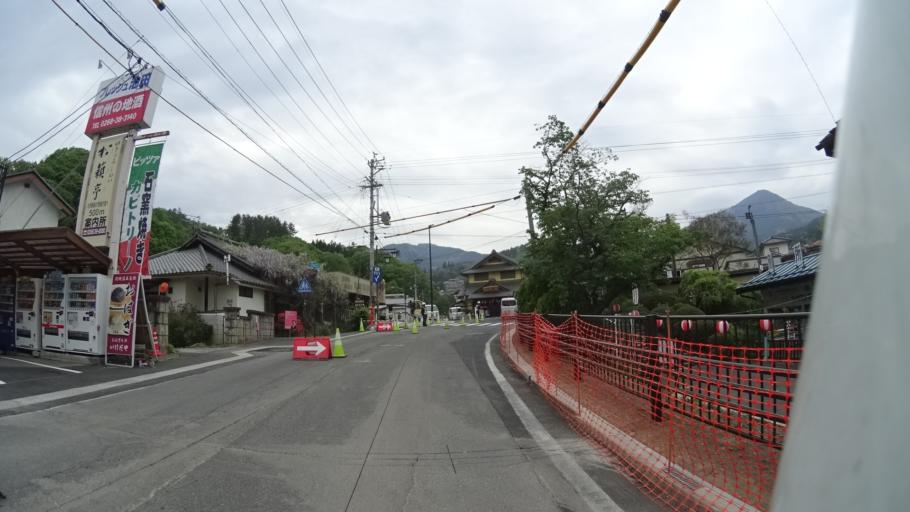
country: JP
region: Nagano
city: Kamimaruko
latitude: 36.3529
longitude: 138.1618
